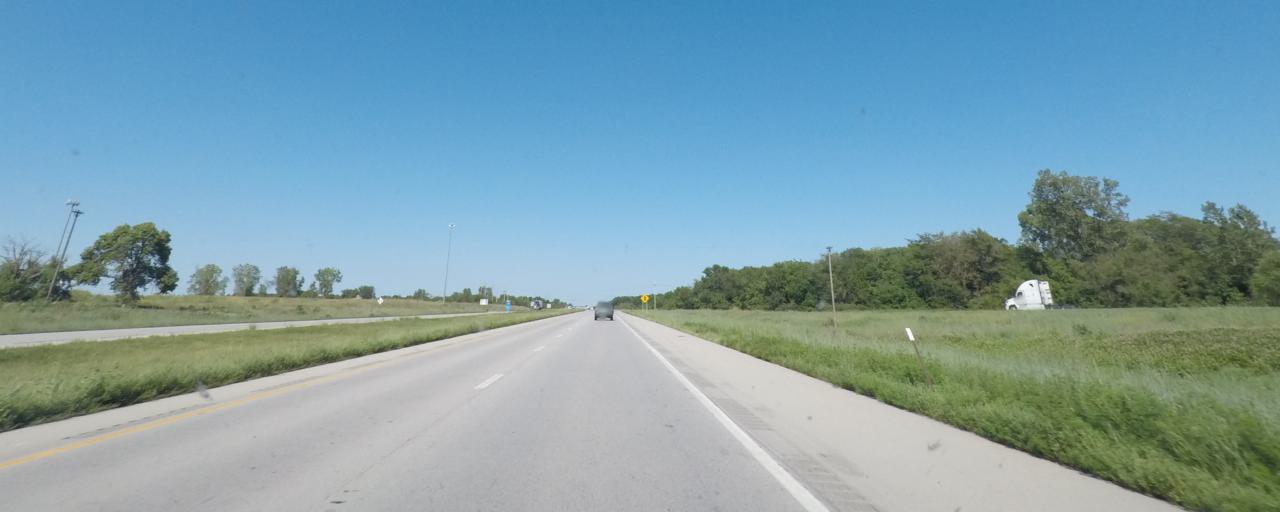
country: US
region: Kansas
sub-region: Johnson County
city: Gardner
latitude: 38.7820
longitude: -94.9255
